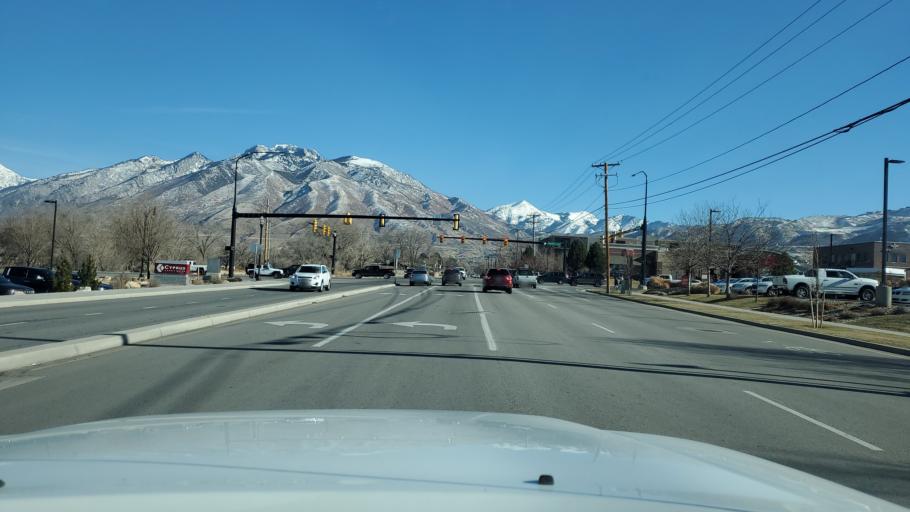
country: US
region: Utah
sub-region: Salt Lake County
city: Draper
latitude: 40.5007
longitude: -111.8860
